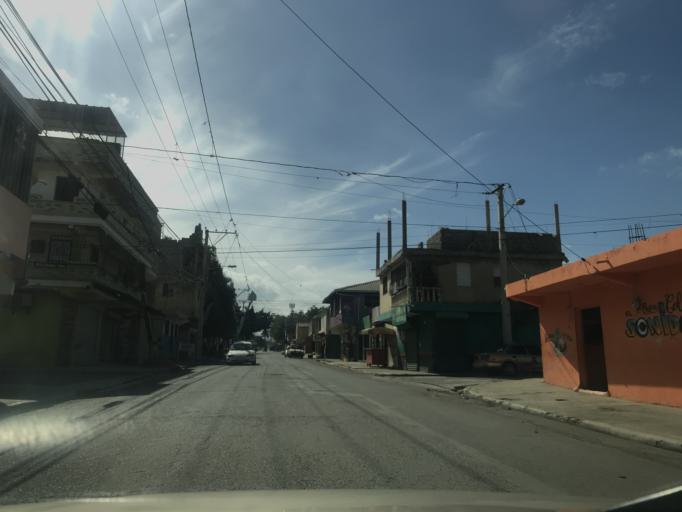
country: DO
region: Santiago
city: Palmar Arriba
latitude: 19.4814
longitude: -70.7483
